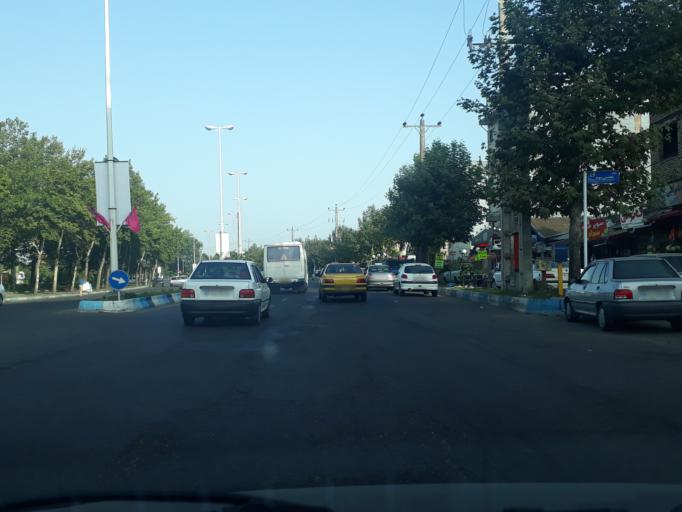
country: IR
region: Gilan
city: Bandar-e Anzali
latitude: 37.4599
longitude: 49.4961
